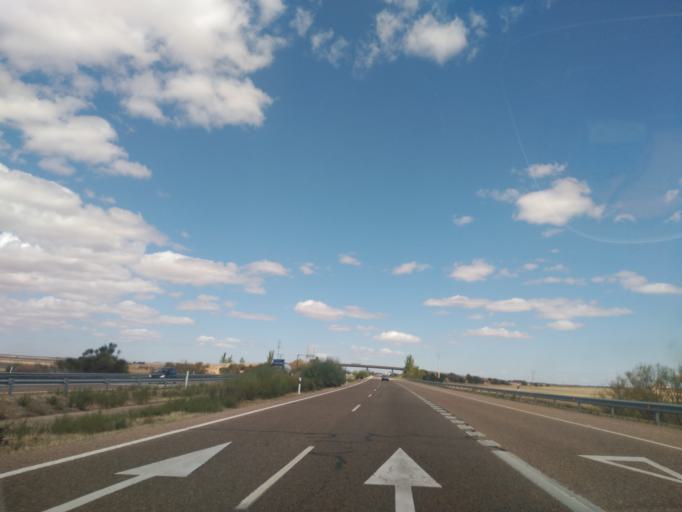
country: ES
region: Castille and Leon
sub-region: Provincia de Salamanca
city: Pedrosillo el Ralo
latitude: 41.0591
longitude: -5.5410
